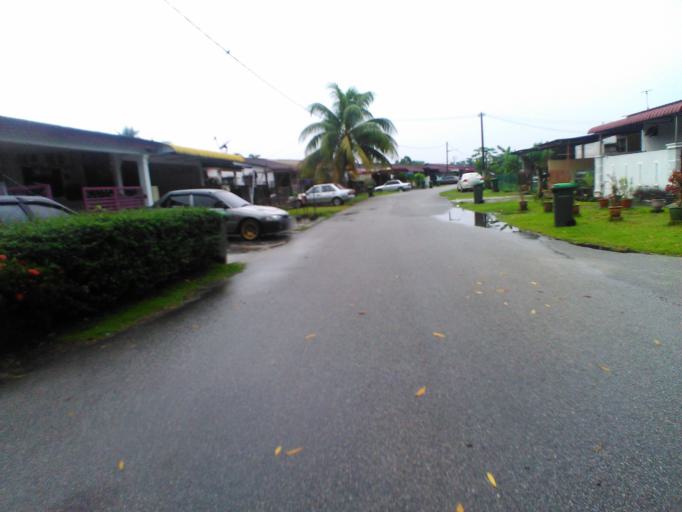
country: MY
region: Kedah
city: Kulim
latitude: 5.3620
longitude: 100.5741
